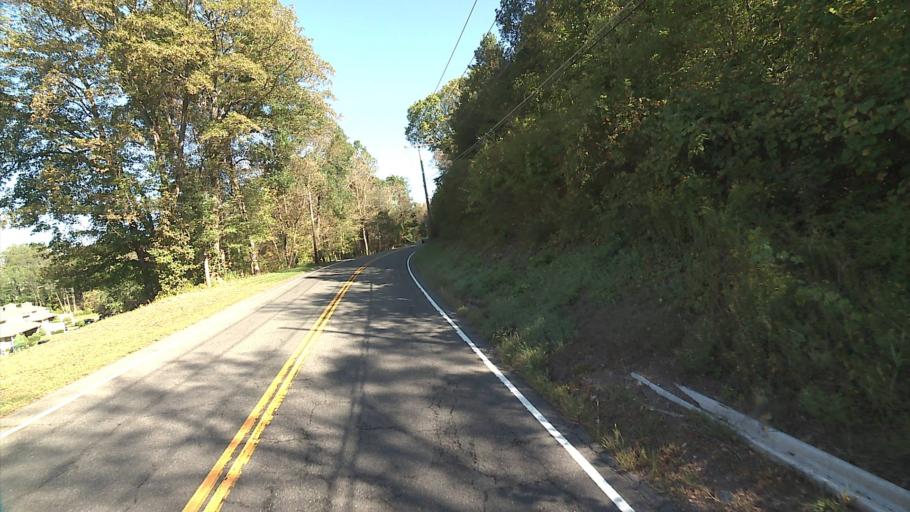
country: US
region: Connecticut
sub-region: Tolland County
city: Somers
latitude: 41.9464
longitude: -72.4496
